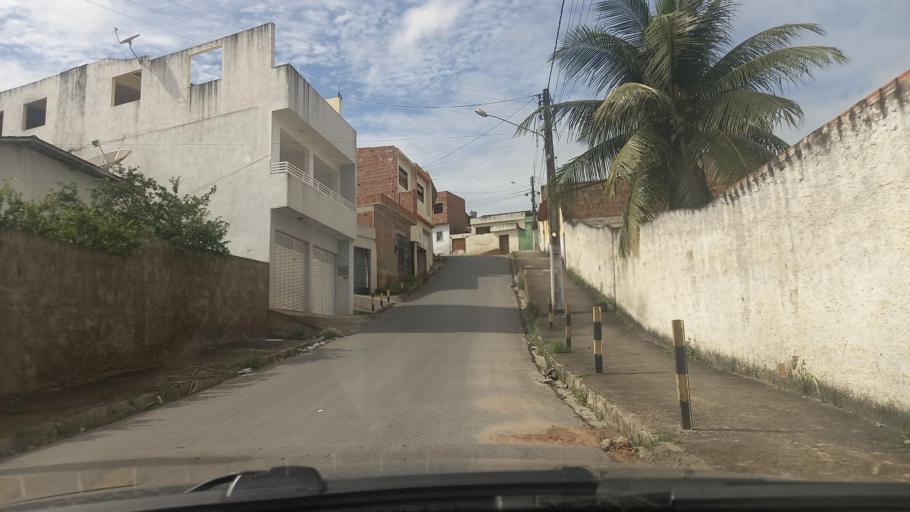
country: BR
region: Pernambuco
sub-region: Vitoria De Santo Antao
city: Vitoria de Santo Antao
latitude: -8.1225
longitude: -35.2895
